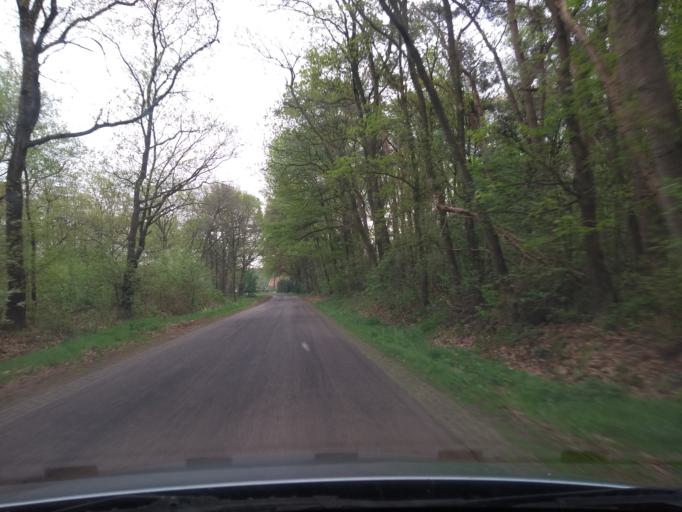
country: DE
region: Lower Saxony
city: Lage
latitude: 52.4221
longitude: 6.9094
